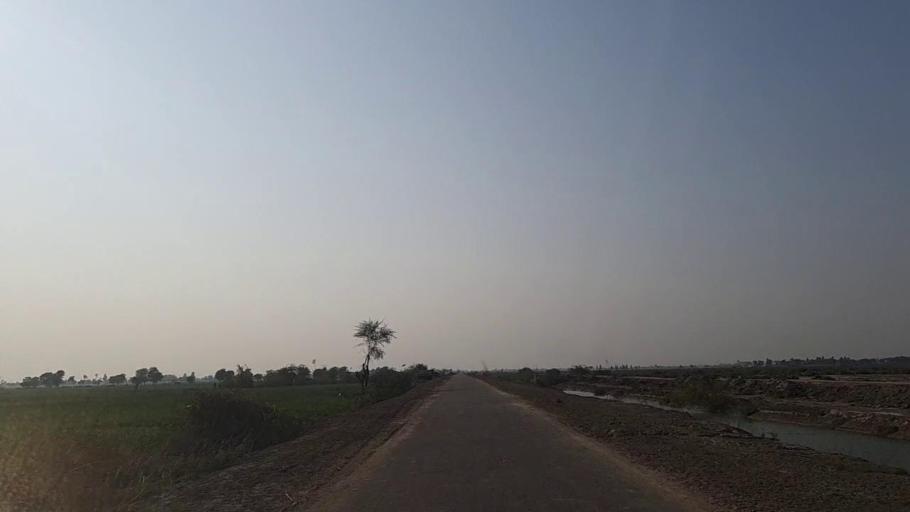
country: PK
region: Sindh
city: Jam Sahib
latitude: 26.2855
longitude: 68.6215
